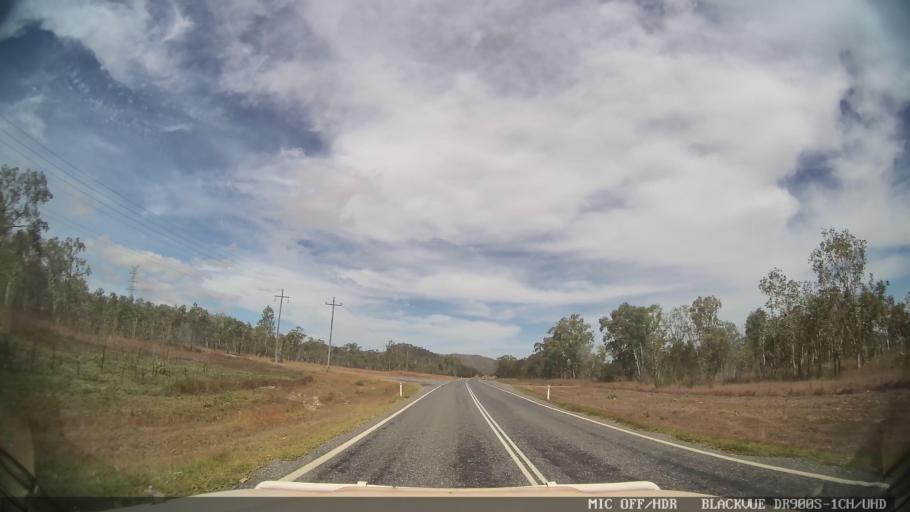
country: AU
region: Queensland
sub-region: Tablelands
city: Mareeba
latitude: -16.7869
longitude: 145.3515
